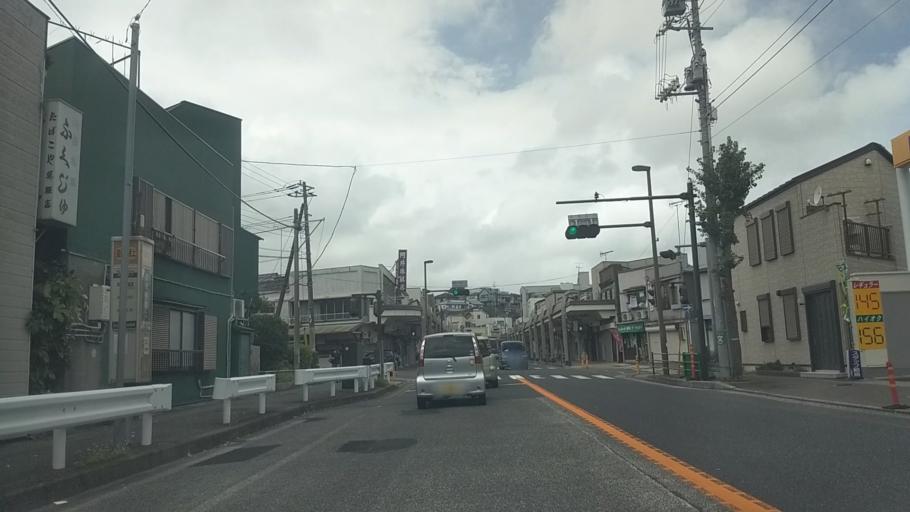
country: JP
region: Kanagawa
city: Yokosuka
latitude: 35.2718
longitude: 139.6716
